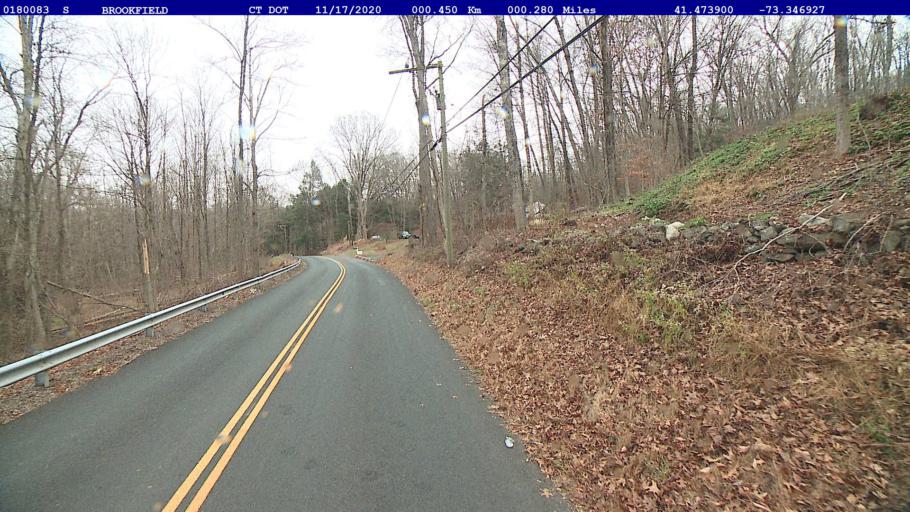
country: US
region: Connecticut
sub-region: Fairfield County
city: Newtown
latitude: 41.4739
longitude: -73.3469
